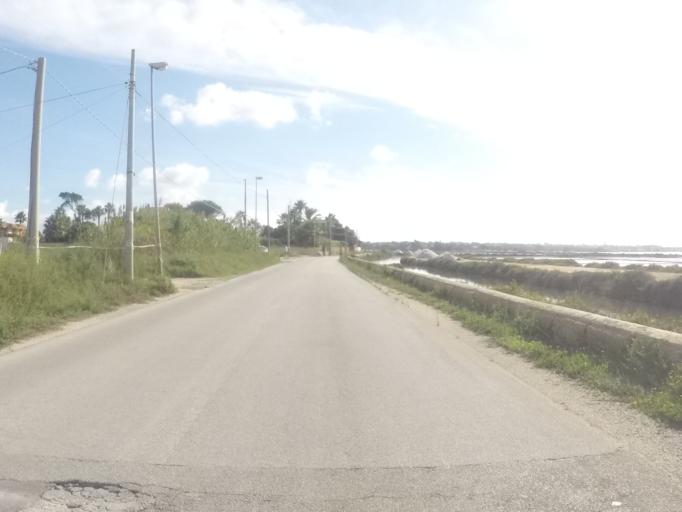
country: IT
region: Sicily
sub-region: Trapani
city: Marsala
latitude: 37.8244
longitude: 12.4682
